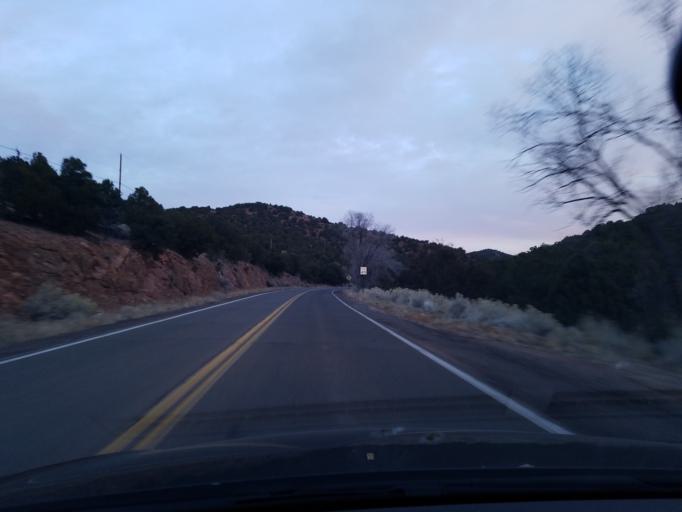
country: US
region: New Mexico
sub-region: Santa Fe County
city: Santa Fe
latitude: 35.7031
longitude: -105.9058
